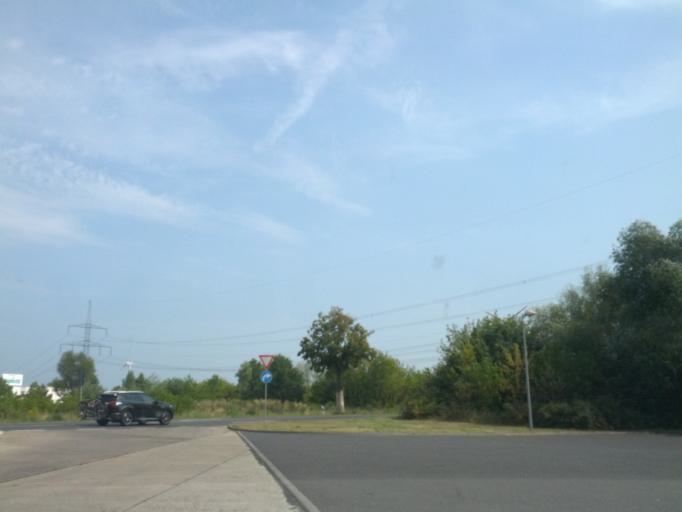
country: DE
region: Brandenburg
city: Nauen
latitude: 52.5955
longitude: 12.8874
